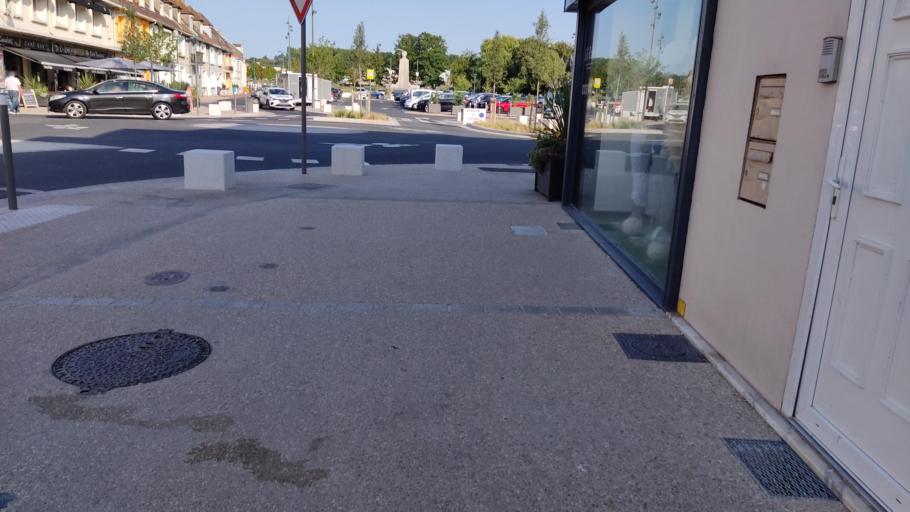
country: FR
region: Nord-Pas-de-Calais
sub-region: Departement du Pas-de-Calais
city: Le Portel
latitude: 50.7070
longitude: 1.5742
